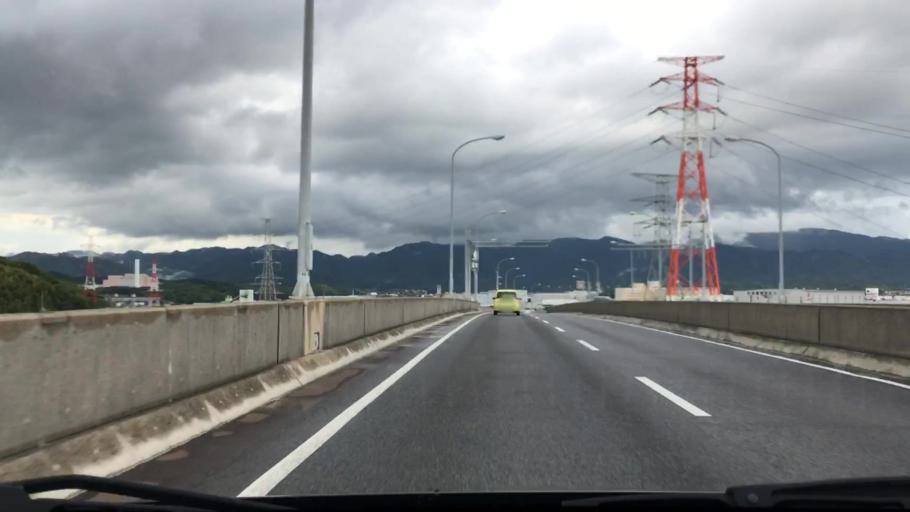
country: JP
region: Fukuoka
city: Fukuoka-shi
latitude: 33.6278
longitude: 130.4720
